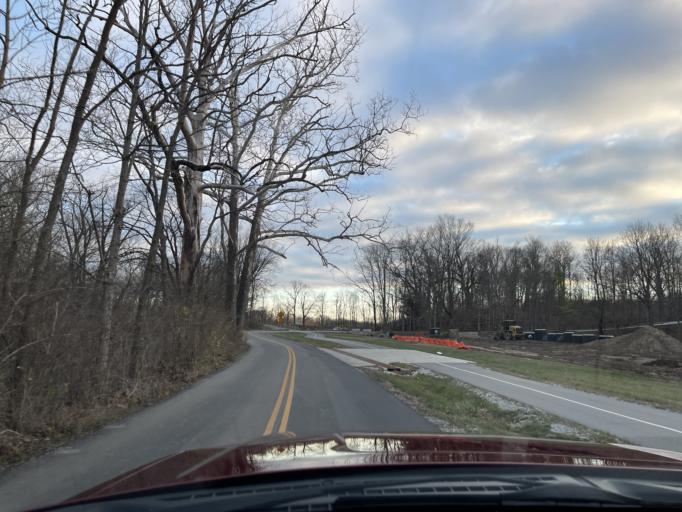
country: US
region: Indiana
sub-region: Hendricks County
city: Avon
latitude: 39.7746
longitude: -86.4211
